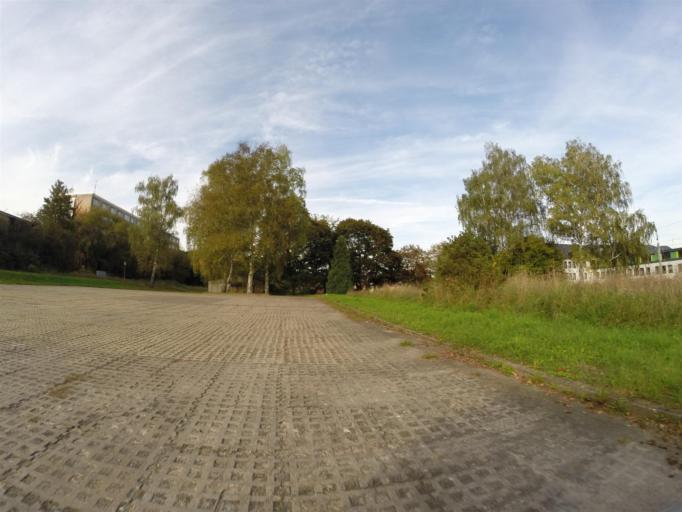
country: DE
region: Thuringia
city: Jena
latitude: 50.9544
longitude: 11.6146
